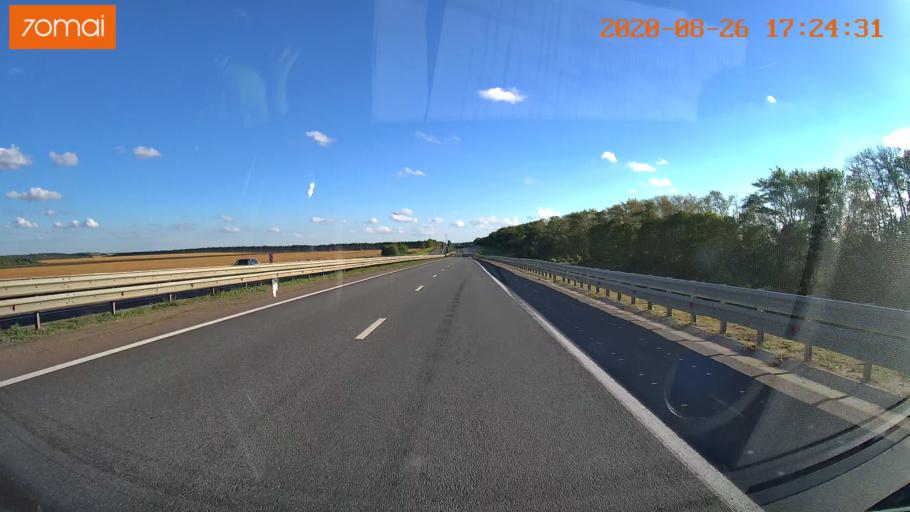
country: RU
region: Tula
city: Volovo
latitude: 53.5167
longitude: 38.1159
